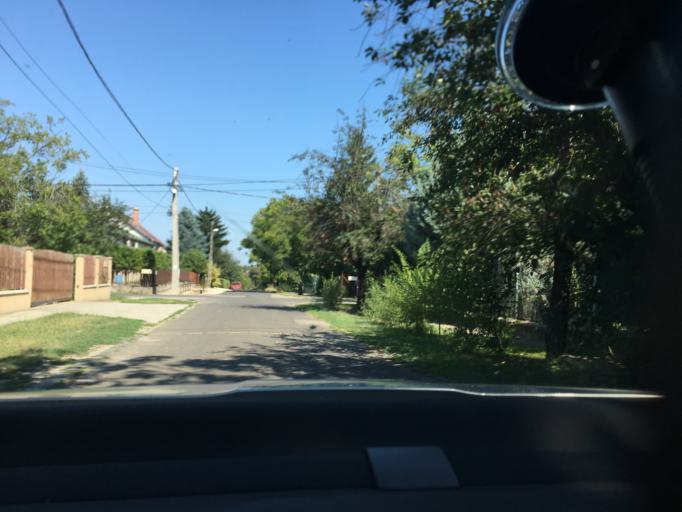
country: HU
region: Budapest
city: Budapest XVI. keruelet
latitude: 47.5057
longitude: 19.1860
